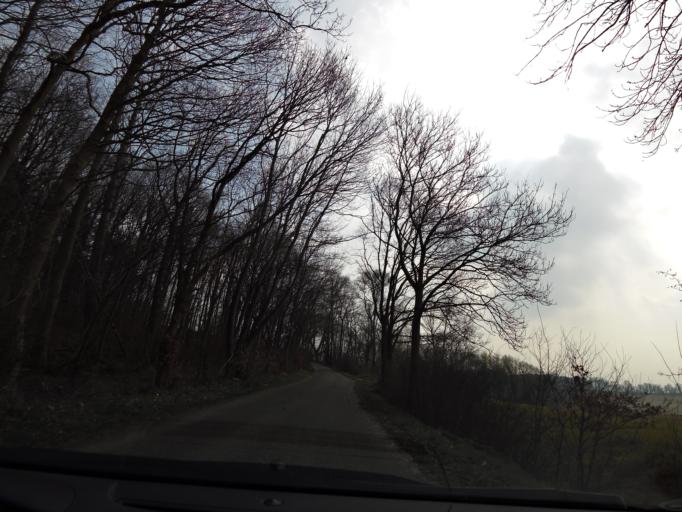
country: NL
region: Limburg
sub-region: Valkenburg aan de Geul
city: Schin op Geul
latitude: 50.8686
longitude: 5.8540
